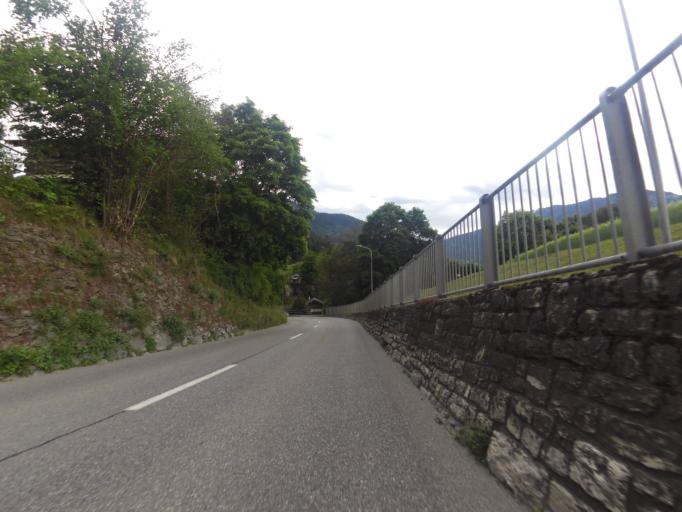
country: CH
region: Grisons
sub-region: Imboden District
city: Tamins
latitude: 46.8257
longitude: 9.4076
